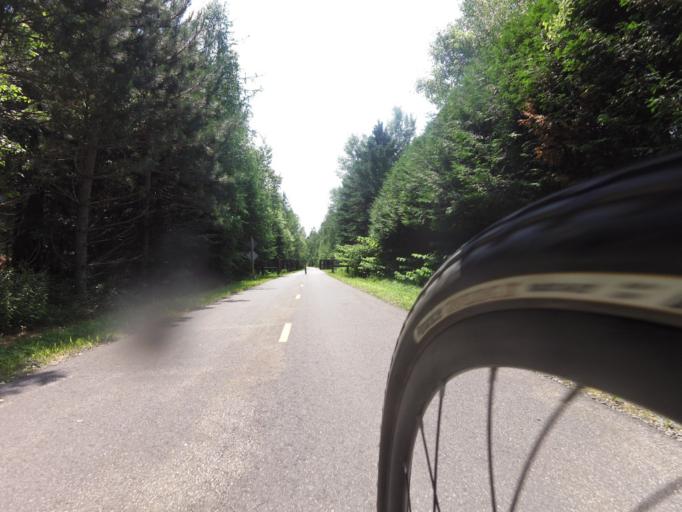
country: CA
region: Quebec
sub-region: Laurentides
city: Mont-Tremblant
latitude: 46.1374
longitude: -74.5966
